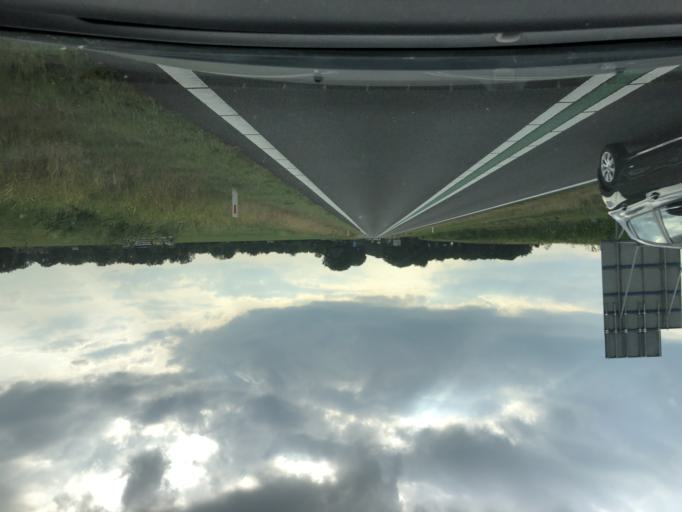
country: NL
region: Drenthe
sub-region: Gemeente Hoogeveen
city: Hoogeveen
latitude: 52.6060
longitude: 6.4449
